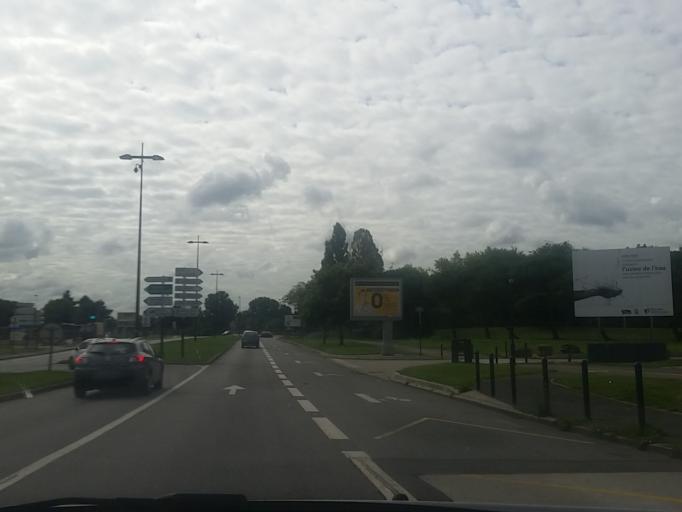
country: FR
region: Pays de la Loire
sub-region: Departement de la Loire-Atlantique
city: Saint-Sebastien-sur-Loire
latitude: 47.2201
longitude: -1.5167
